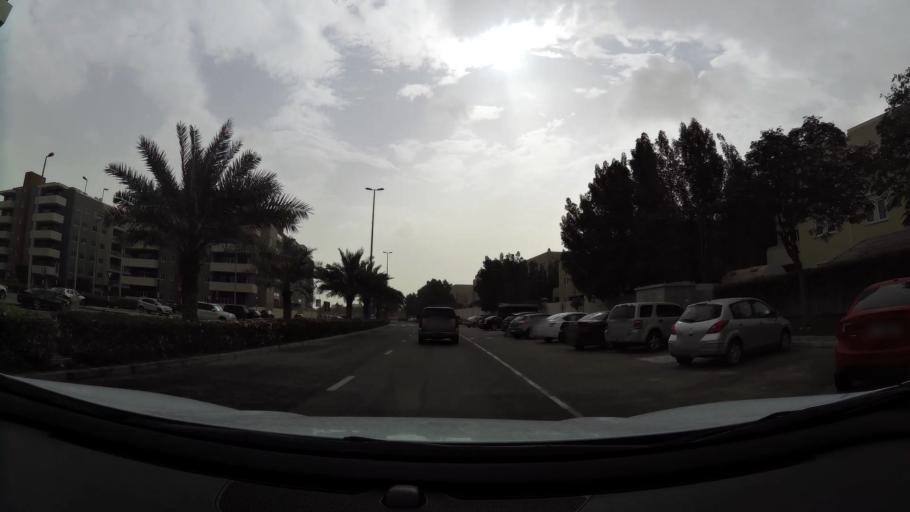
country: AE
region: Abu Dhabi
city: Abu Dhabi
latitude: 24.4546
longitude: 54.6717
